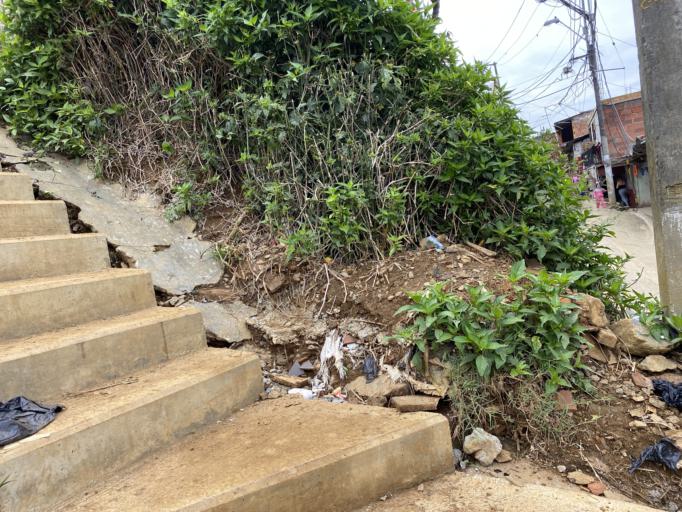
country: CO
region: Antioquia
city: Medellin
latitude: 6.2650
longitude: -75.5408
